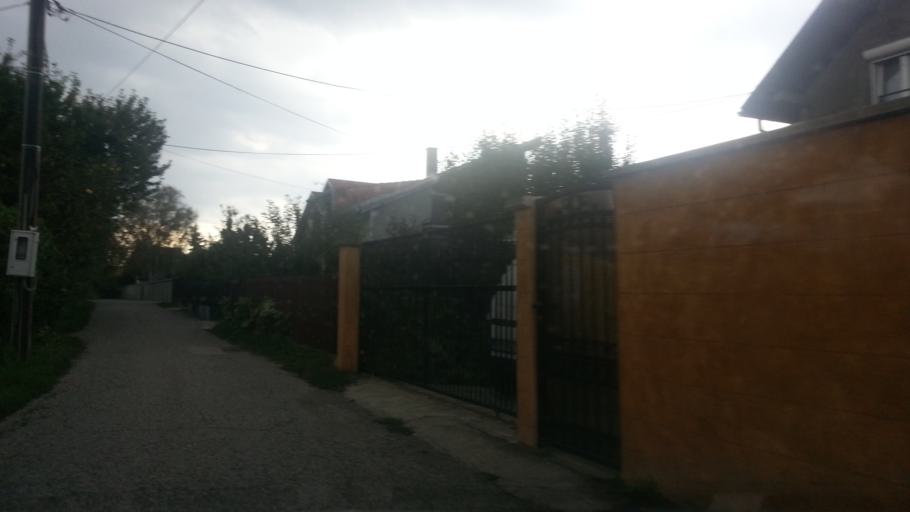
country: RS
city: Novi Banovci
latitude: 44.9627
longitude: 20.2781
